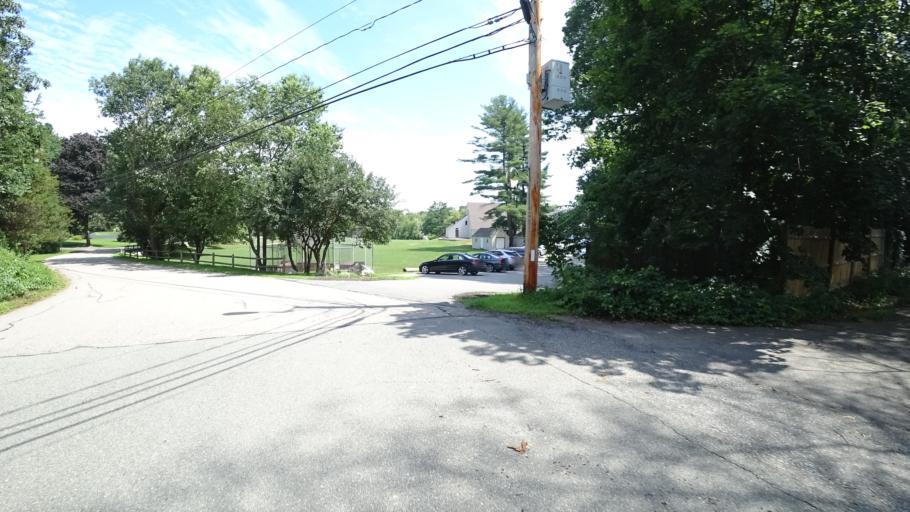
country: US
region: Massachusetts
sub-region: Norfolk County
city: Dedham
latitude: 42.2382
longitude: -71.1874
